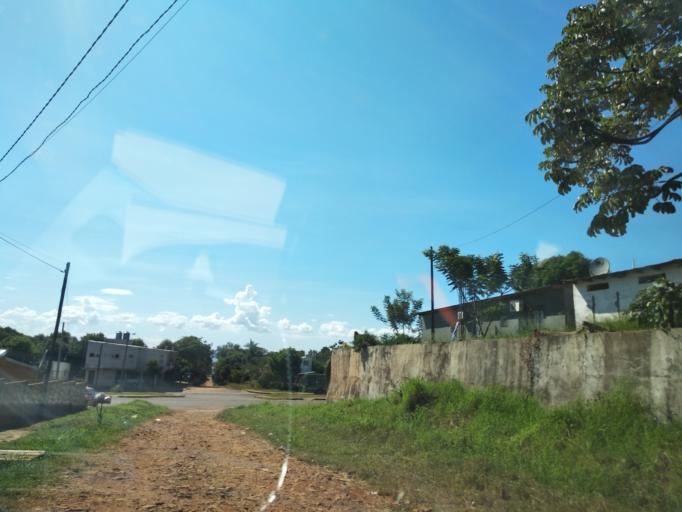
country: AR
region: Misiones
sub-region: Departamento de Capital
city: Posadas
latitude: -27.4274
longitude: -55.8807
